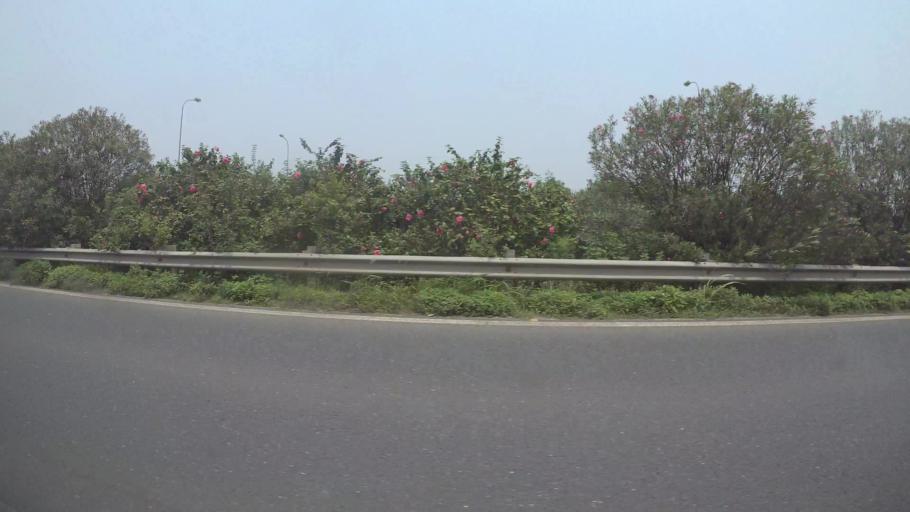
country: VN
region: Ha Noi
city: Troi
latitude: 21.0089
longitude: 105.7066
